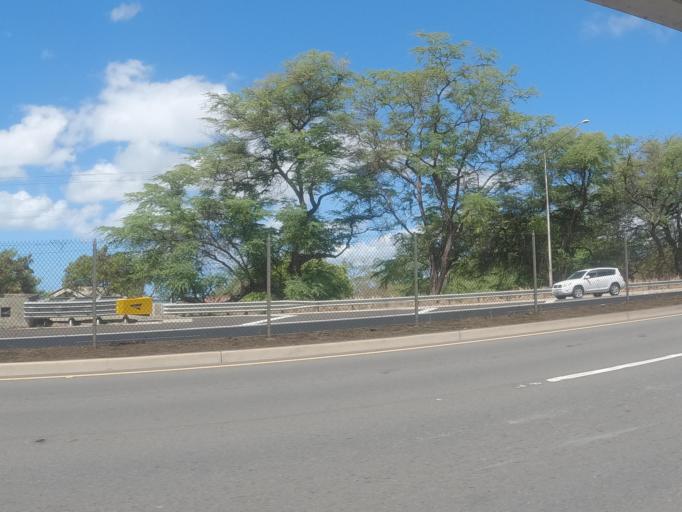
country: US
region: Hawaii
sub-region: Honolulu County
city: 'Aiea
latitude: 21.3780
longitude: -157.9353
